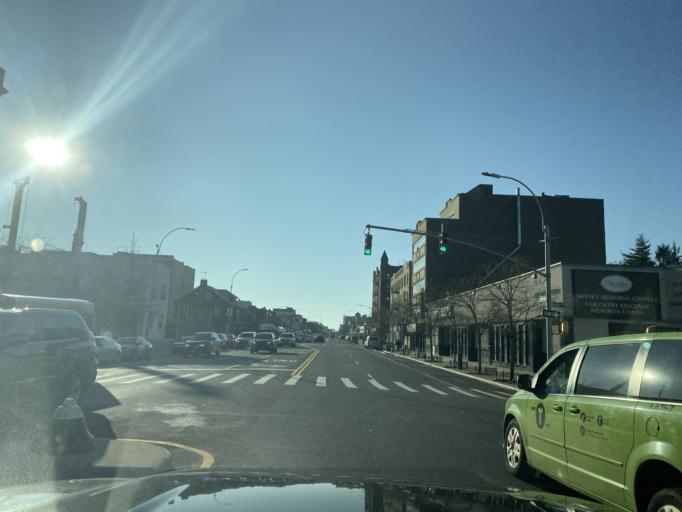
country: US
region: New York
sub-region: Kings County
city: Bensonhurst
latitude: 40.6164
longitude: -73.9636
